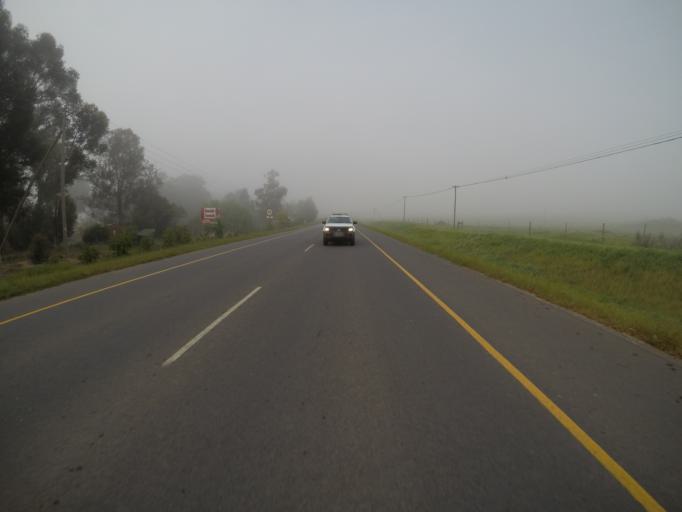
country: ZA
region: Western Cape
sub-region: City of Cape Town
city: Kraaifontein
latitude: -33.7733
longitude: 18.7094
